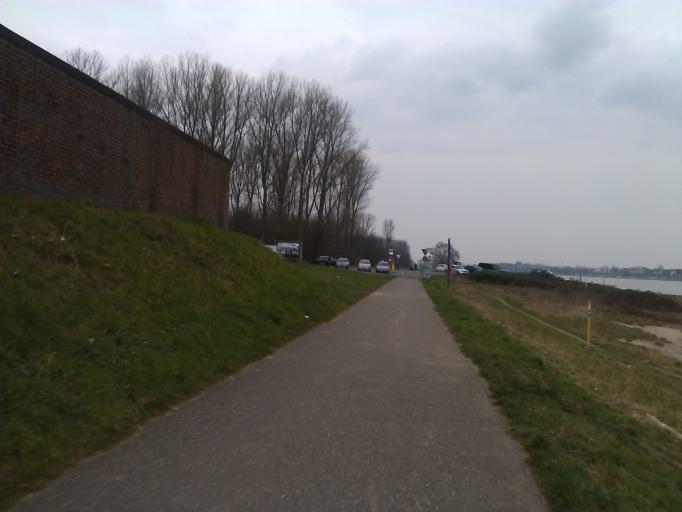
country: DE
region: North Rhine-Westphalia
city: Monheim am Rhein
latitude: 51.0528
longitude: 6.9158
